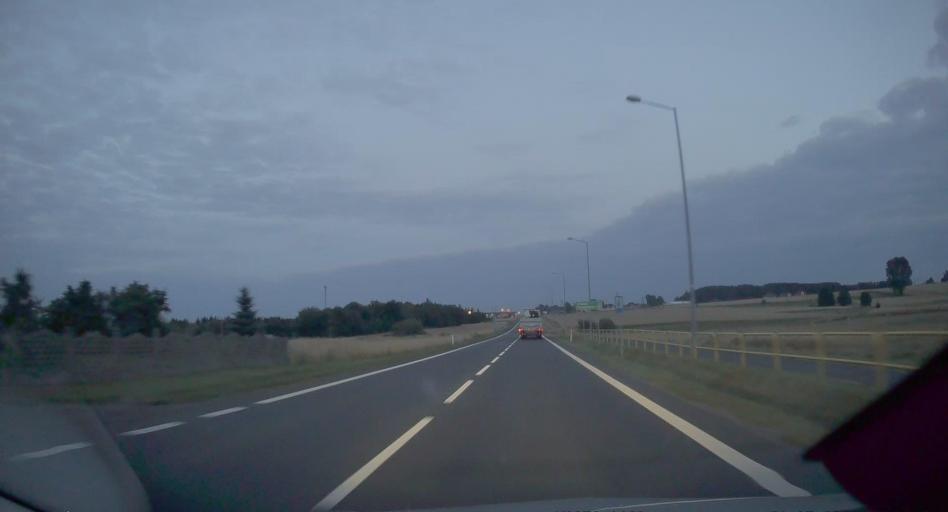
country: PL
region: Silesian Voivodeship
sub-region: Powiat klobucki
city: Opatow
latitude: 50.9336
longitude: 18.8534
